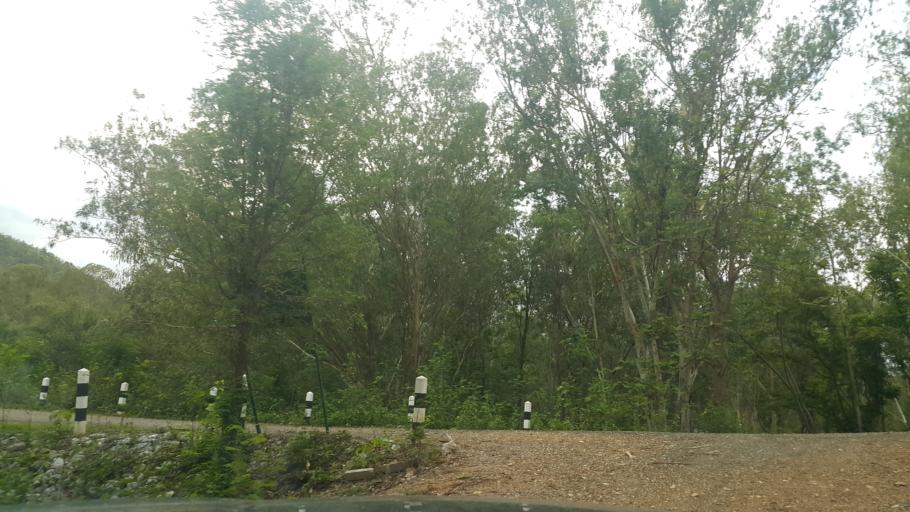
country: TH
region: Chiang Mai
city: Mae On
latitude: 18.7157
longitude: 99.2366
